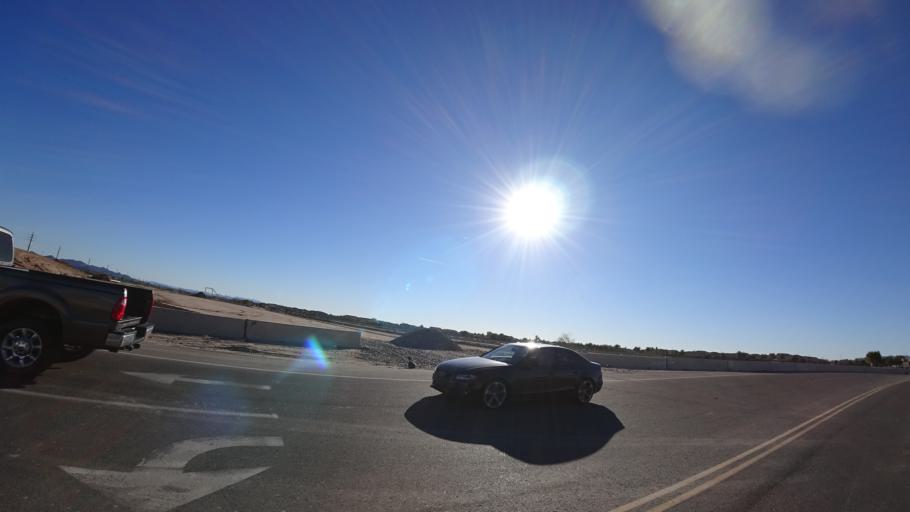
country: US
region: Arizona
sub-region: Maricopa County
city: Goodyear
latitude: 33.4493
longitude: -112.4275
